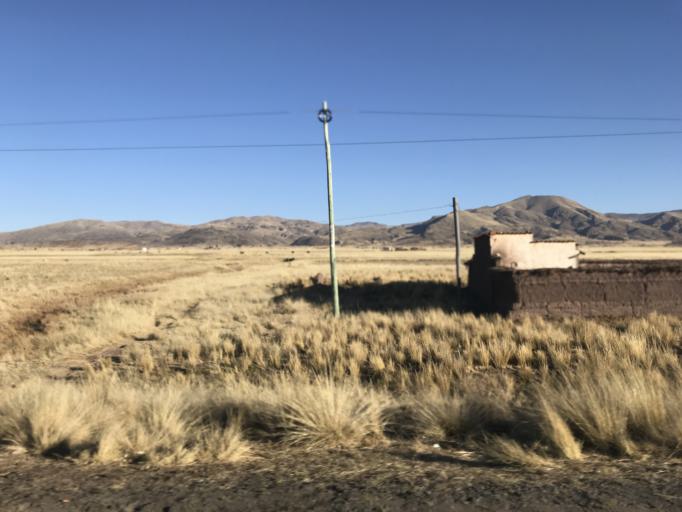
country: BO
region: La Paz
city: Tiahuanaco
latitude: -16.5688
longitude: -68.6594
